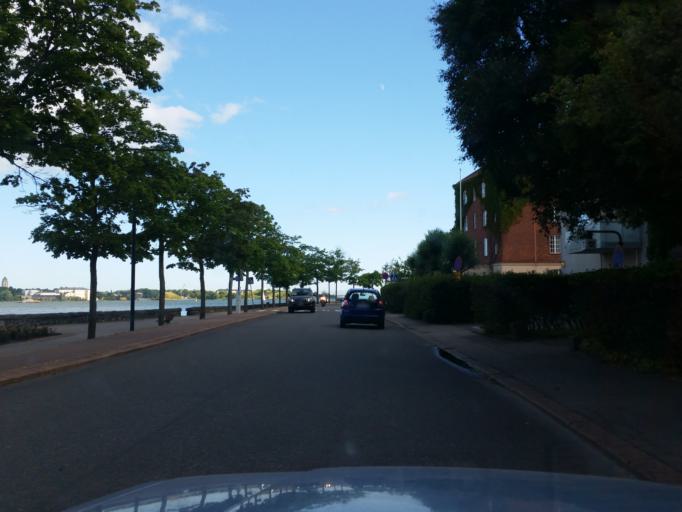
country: FI
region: Uusimaa
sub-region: Helsinki
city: Helsinki
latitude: 60.1584
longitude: 24.9618
